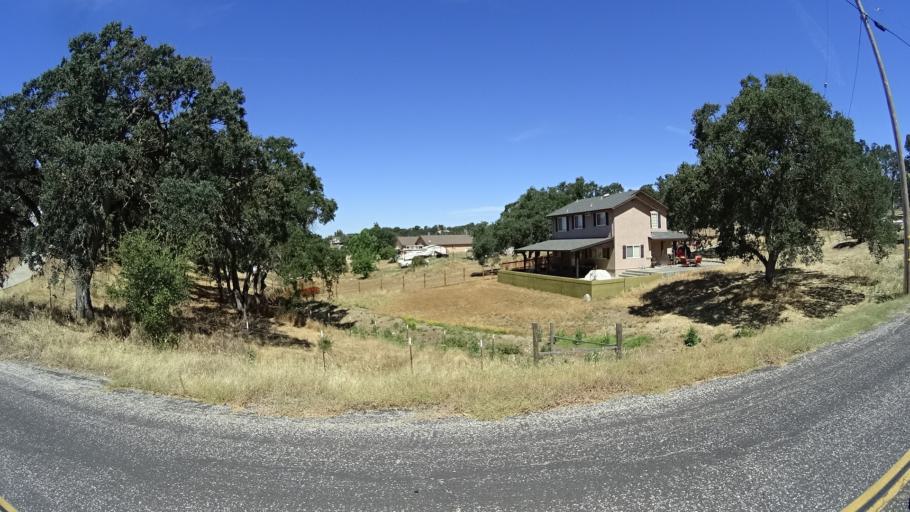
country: US
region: California
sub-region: Calaveras County
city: Valley Springs
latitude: 38.1583
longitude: -120.8336
